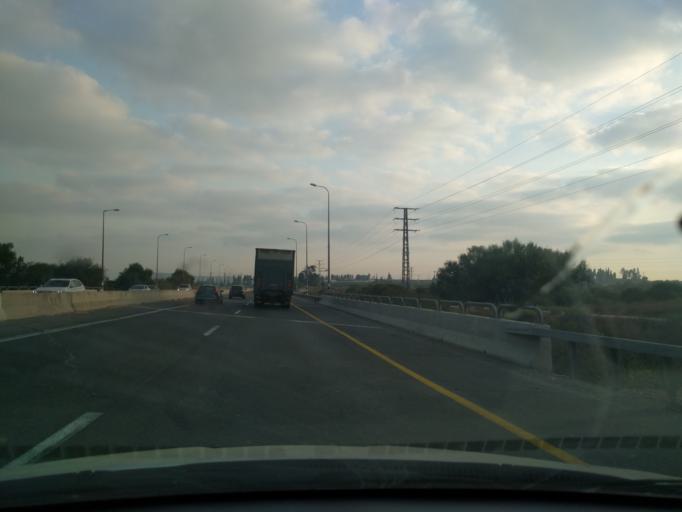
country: IL
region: Haifa
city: Qesarya
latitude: 32.5034
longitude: 34.9294
